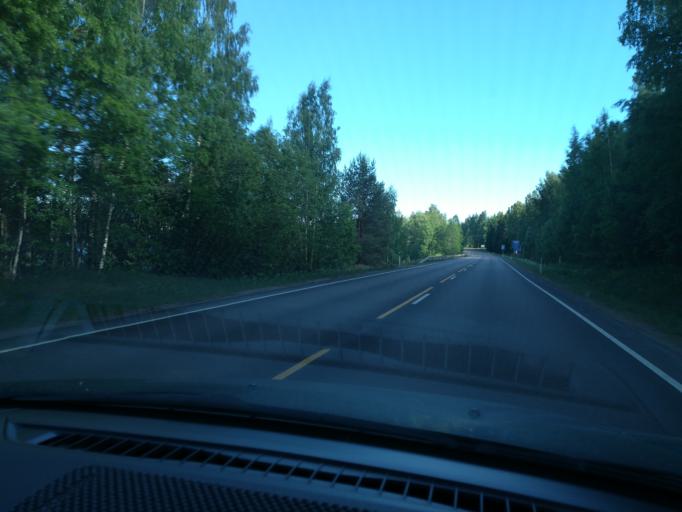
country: FI
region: Southern Savonia
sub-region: Mikkeli
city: Puumala
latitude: 61.5135
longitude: 28.1766
